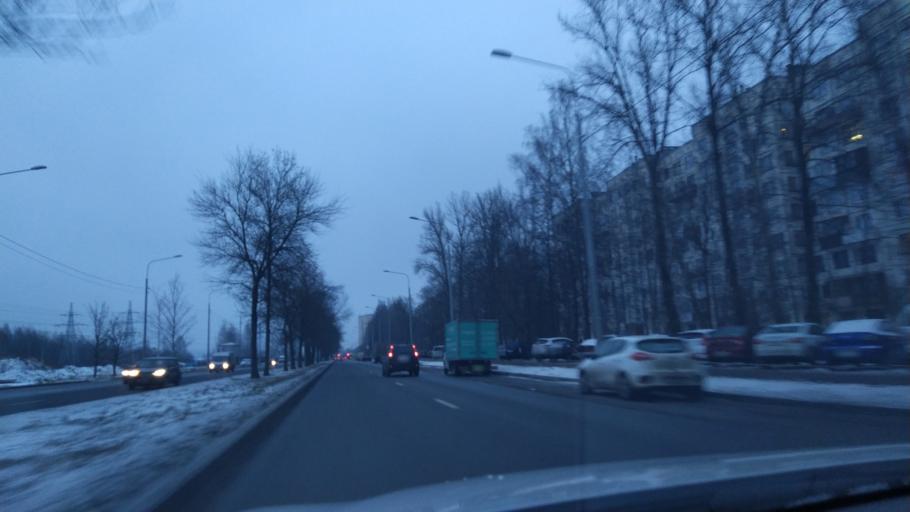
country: RU
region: St.-Petersburg
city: Grazhdanka
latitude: 60.0181
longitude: 30.4215
